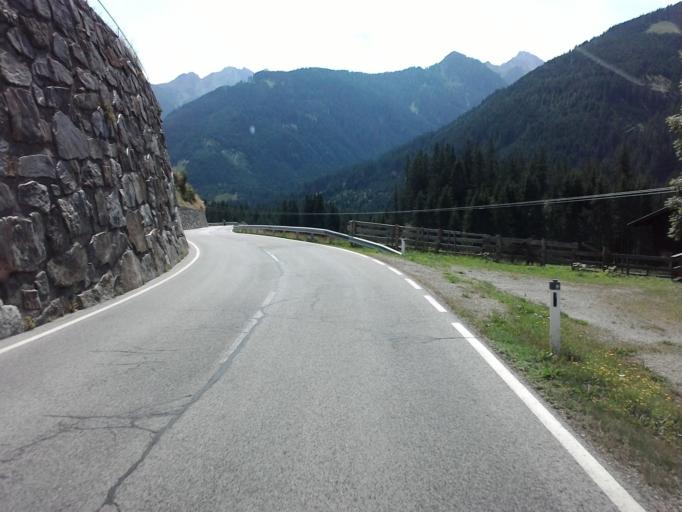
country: AT
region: Tyrol
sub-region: Politischer Bezirk Lienz
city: Obertilliach
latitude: 46.7035
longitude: 12.6433
